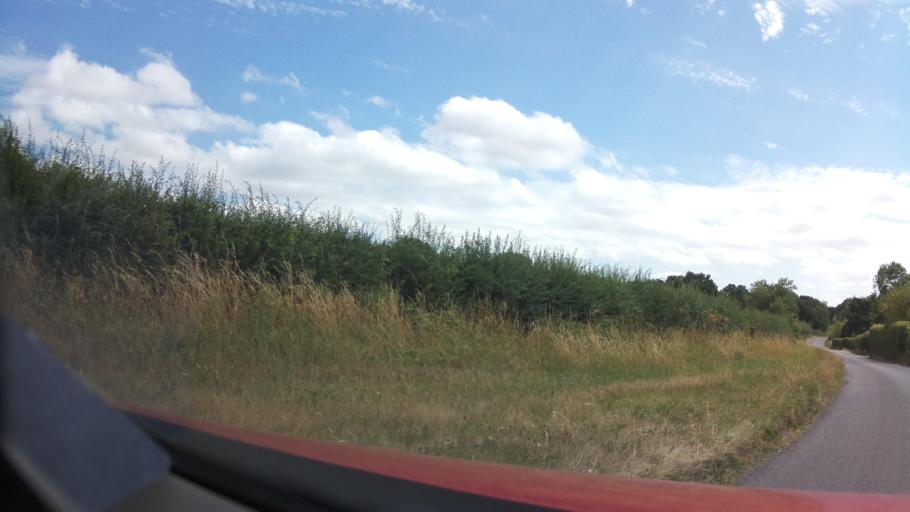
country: GB
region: England
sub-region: Warwickshire
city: Henley in Arden
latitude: 52.2755
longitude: -1.7648
